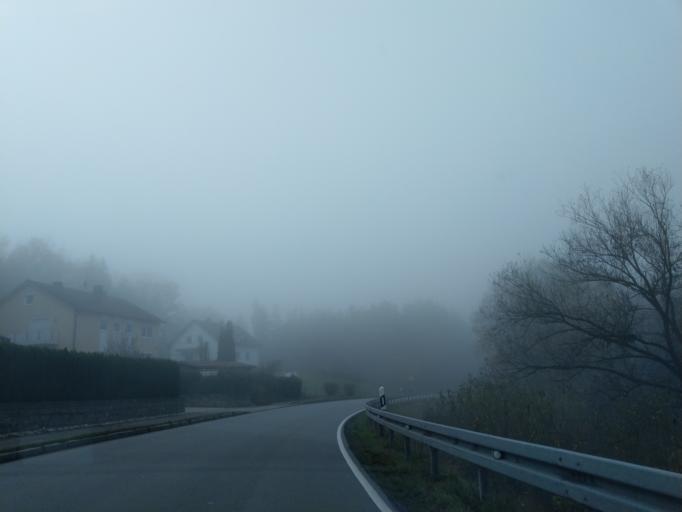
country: DE
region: Bavaria
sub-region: Lower Bavaria
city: Schollnach
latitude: 48.7486
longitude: 13.1694
